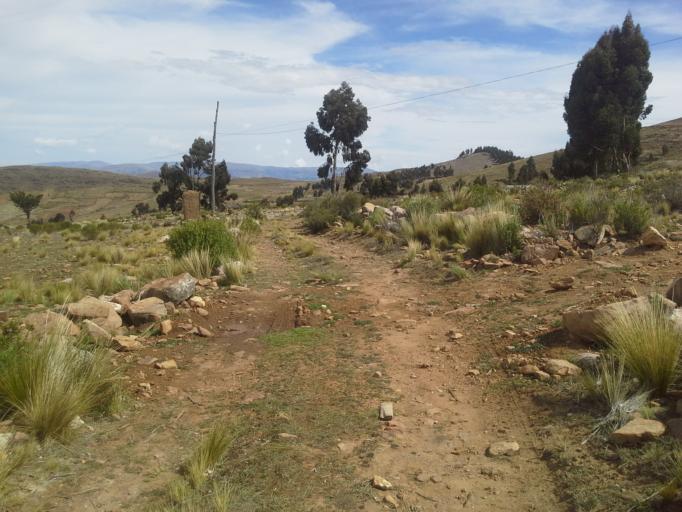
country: BO
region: Cochabamba
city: Colomi
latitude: -17.4384
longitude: -65.8304
